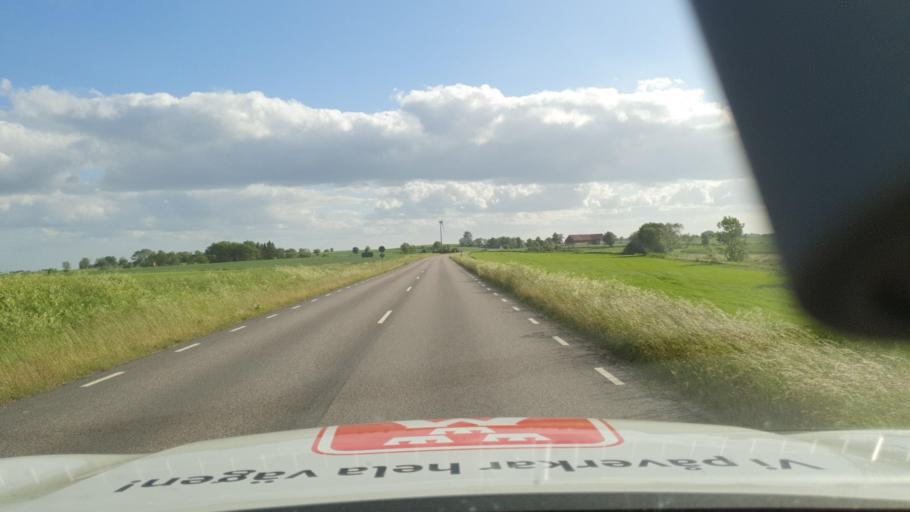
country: SE
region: Skane
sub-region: Tomelilla Kommun
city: Tomelilla
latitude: 55.5761
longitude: 14.0022
